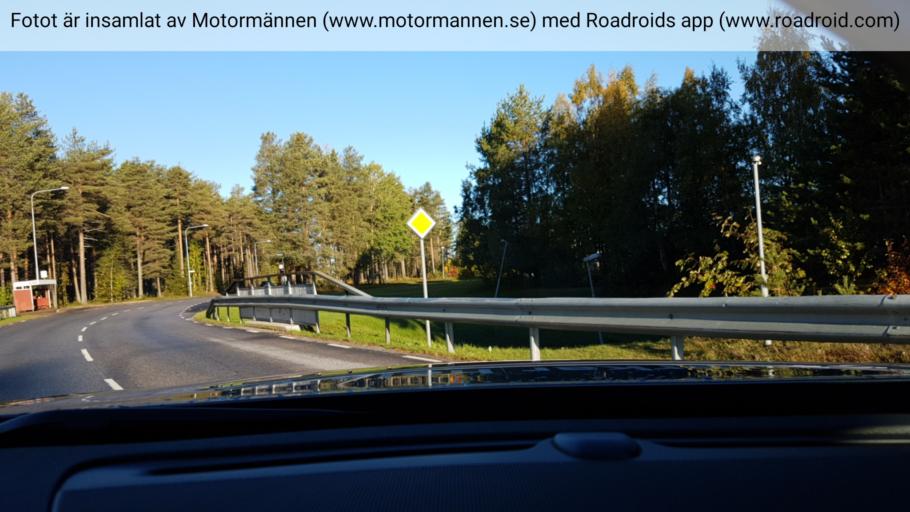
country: SE
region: Norrbotten
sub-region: Lulea Kommun
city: Sodra Sunderbyn
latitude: 65.6503
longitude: 21.9563
